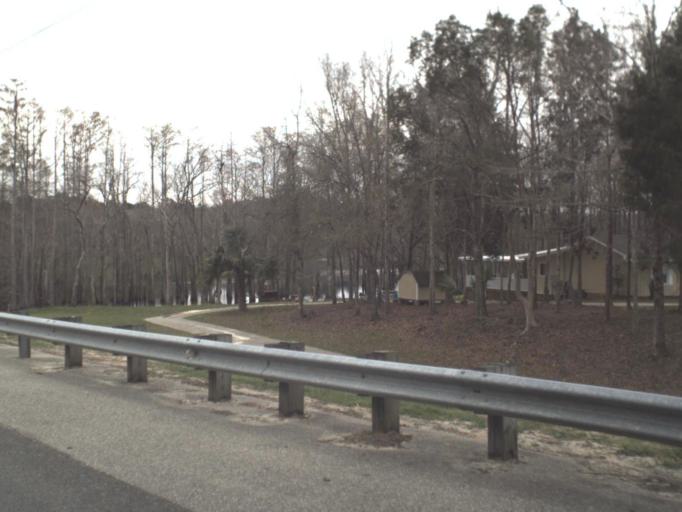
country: US
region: Florida
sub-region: Gulf County
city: Wewahitchka
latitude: 30.1323
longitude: -85.2072
